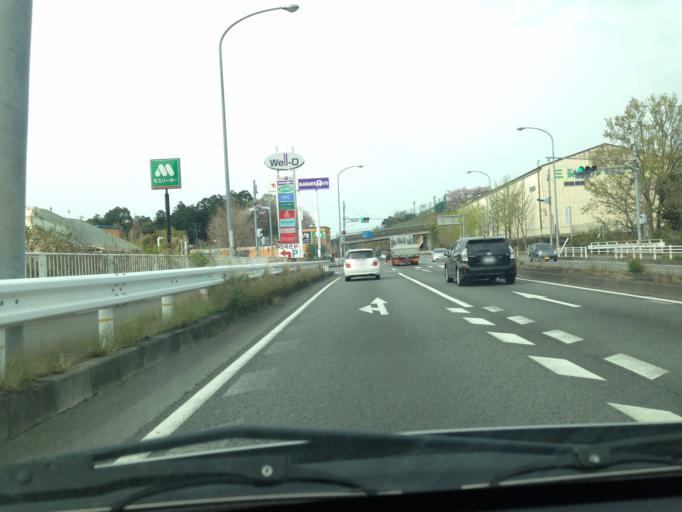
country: JP
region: Shizuoka
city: Mishima
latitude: 35.1498
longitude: 138.8918
